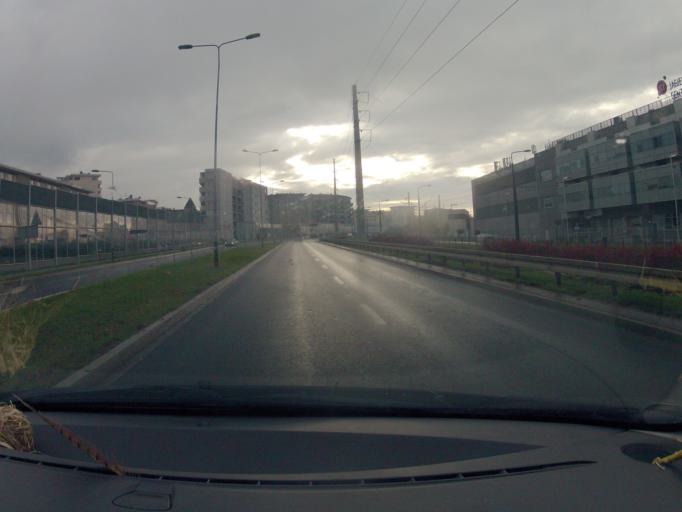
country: PL
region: Lesser Poland Voivodeship
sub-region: Krakow
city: Sidzina
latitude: 50.0199
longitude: 19.8974
